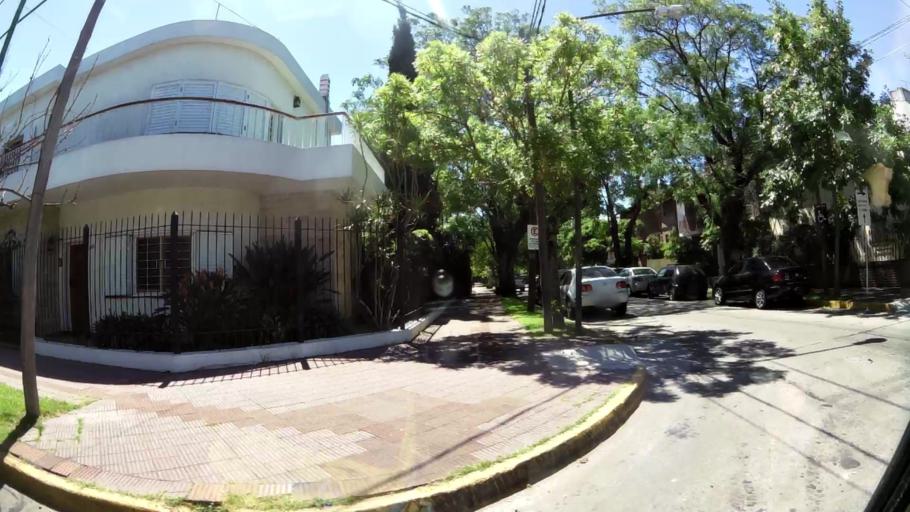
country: AR
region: Buenos Aires
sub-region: Partido de San Isidro
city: San Isidro
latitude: -34.4790
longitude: -58.5021
